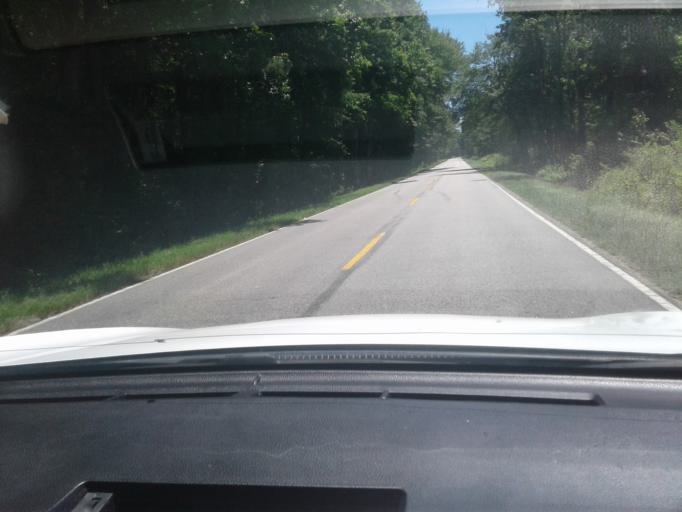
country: US
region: North Carolina
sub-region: Harnett County
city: Erwin
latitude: 35.3246
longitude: -78.7233
